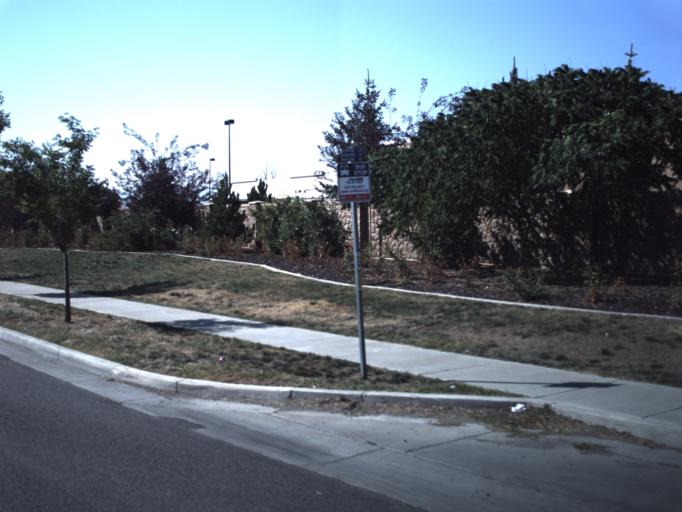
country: US
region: Utah
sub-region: Cache County
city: River Heights
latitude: 41.7126
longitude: -111.8348
